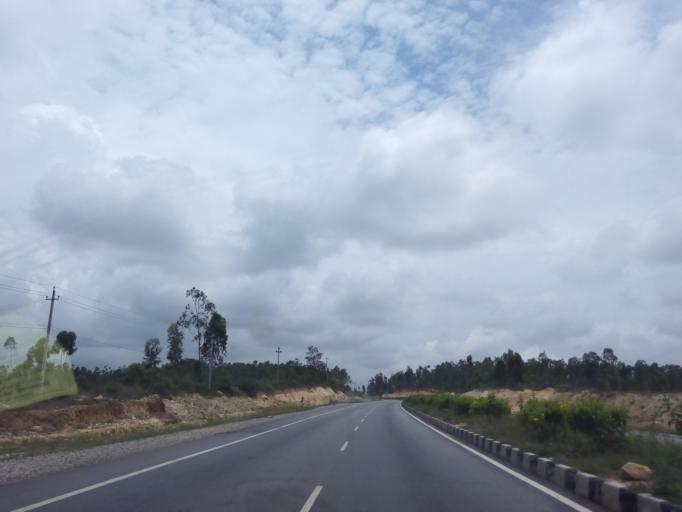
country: IN
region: Karnataka
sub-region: Hassan
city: Hassan
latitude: 12.9915
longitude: 76.1820
